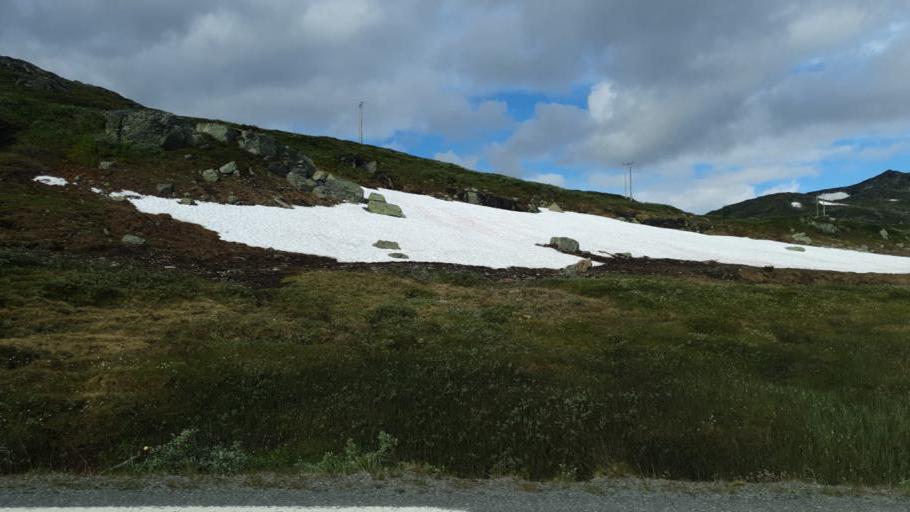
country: NO
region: Oppland
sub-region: Vestre Slidre
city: Slidre
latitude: 61.3226
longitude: 8.8033
